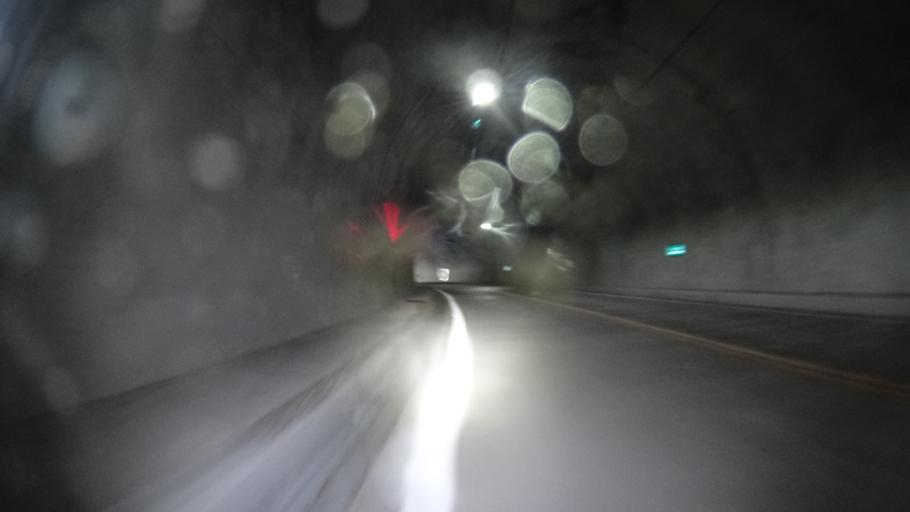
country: JP
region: Yamanashi
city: Enzan
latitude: 35.8024
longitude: 138.8648
